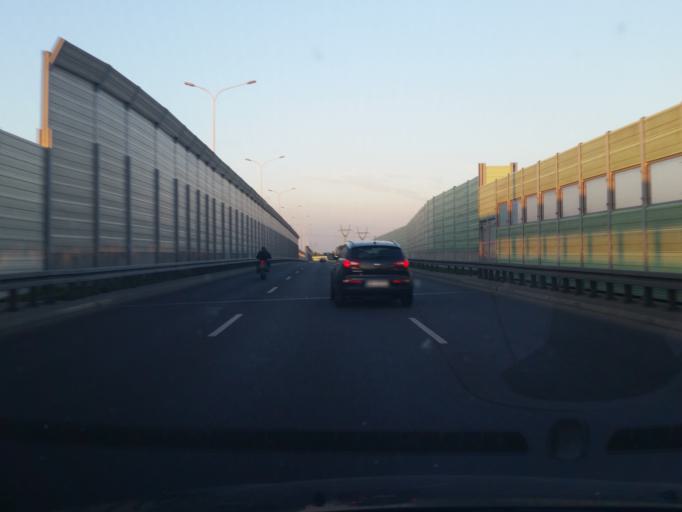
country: PL
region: Masovian Voivodeship
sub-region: Warszawa
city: Bialoleka
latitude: 52.3129
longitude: 20.9662
